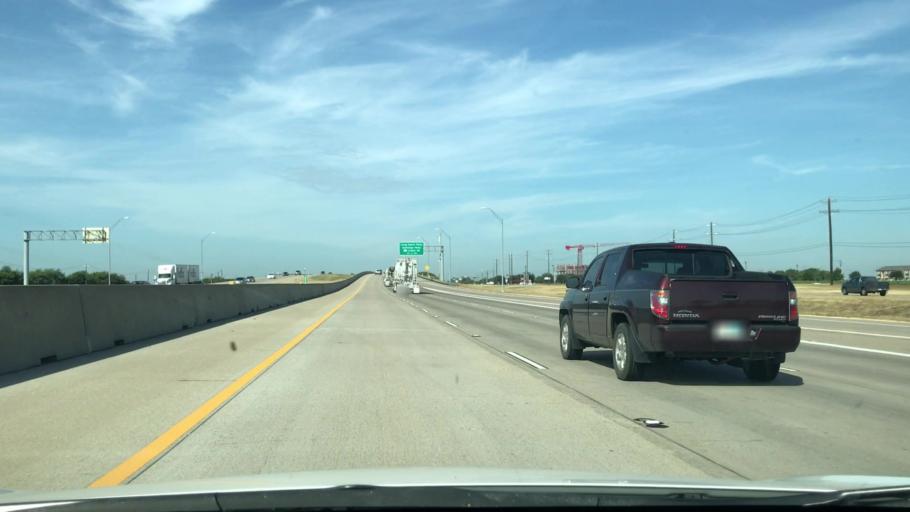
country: US
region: Texas
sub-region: Collin County
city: Allen
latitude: 33.1363
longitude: -96.7017
